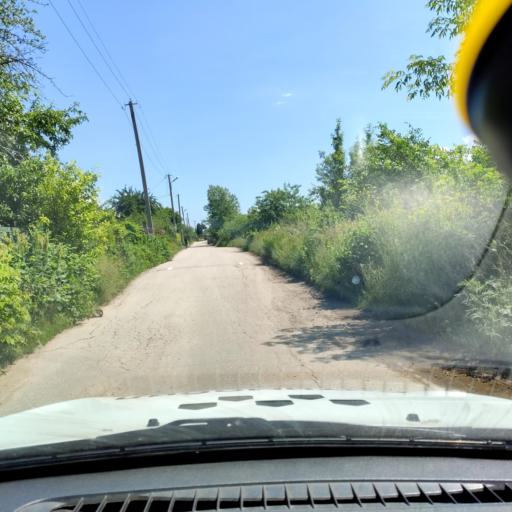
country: RU
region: Samara
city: Povolzhskiy
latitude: 53.4715
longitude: 49.6741
